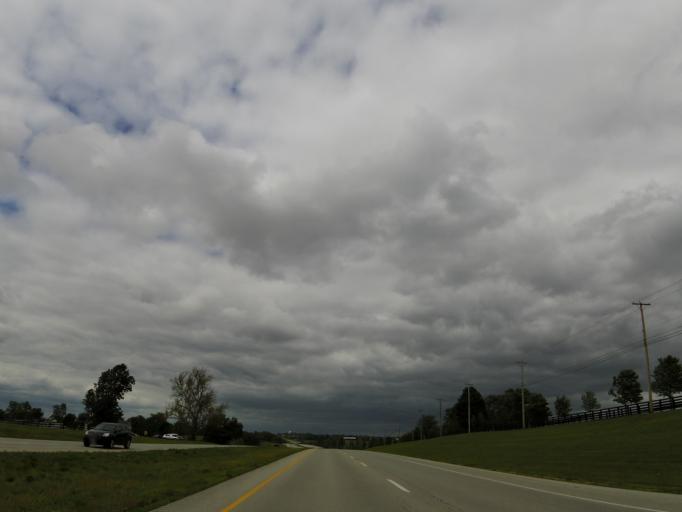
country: US
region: Kentucky
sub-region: Scott County
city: Georgetown
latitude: 38.1781
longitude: -84.5965
